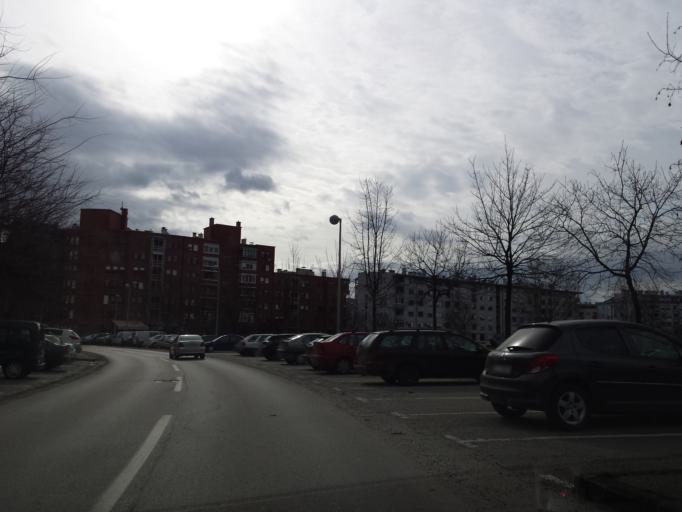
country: HR
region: Grad Zagreb
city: Stenjevec
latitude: 45.8095
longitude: 15.8892
